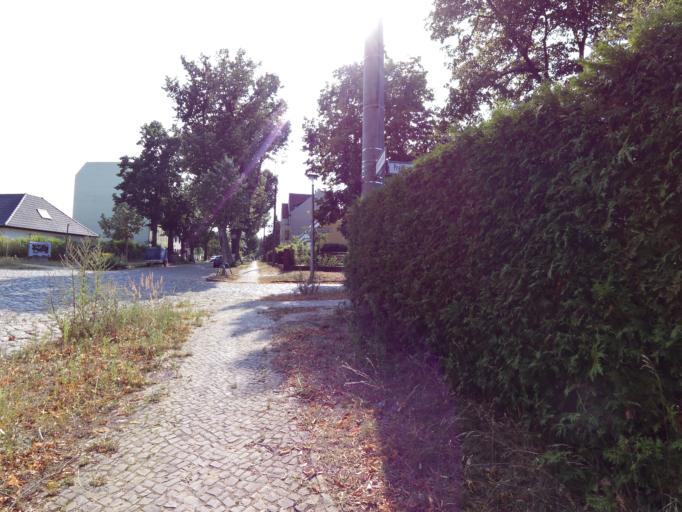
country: DE
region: Berlin
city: Altglienicke
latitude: 52.4127
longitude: 13.5575
